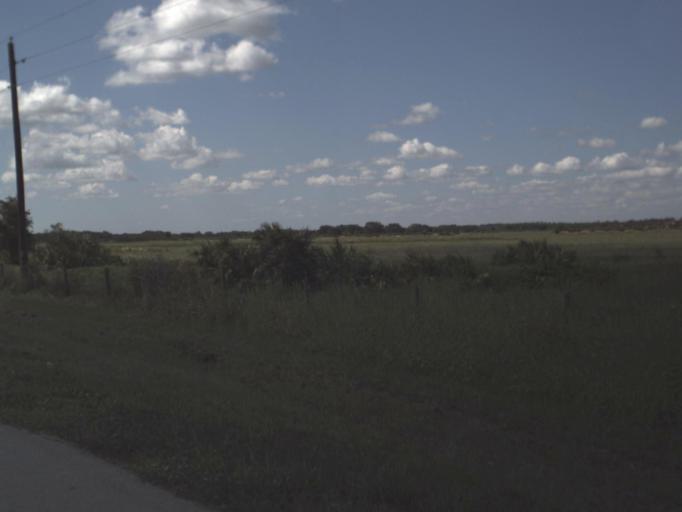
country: US
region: Florida
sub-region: Hendry County
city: Port LaBelle
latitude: 26.8121
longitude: -81.3952
